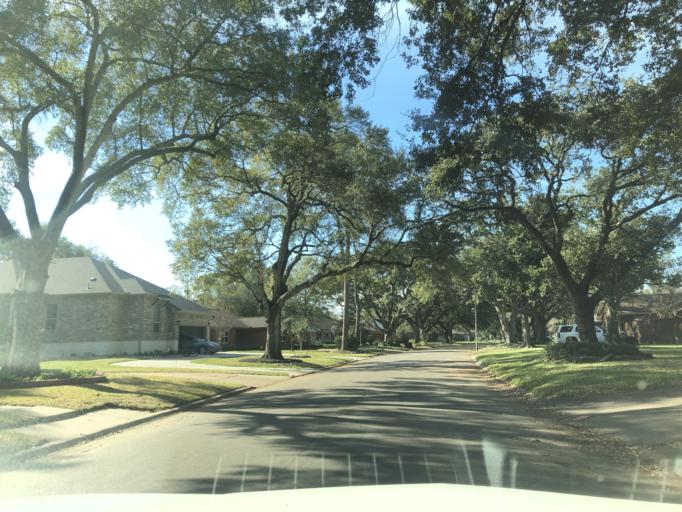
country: US
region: Texas
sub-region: Harris County
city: Bellaire
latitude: 29.6779
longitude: -95.5147
